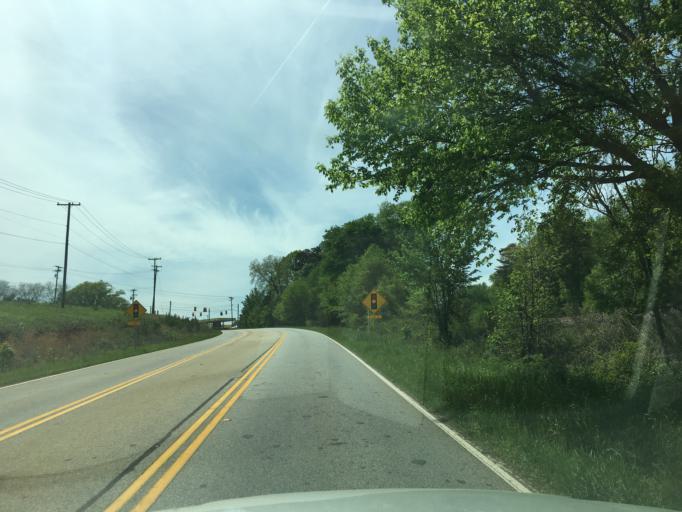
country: US
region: South Carolina
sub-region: Greenville County
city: Taylors
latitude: 34.9173
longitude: -82.2643
